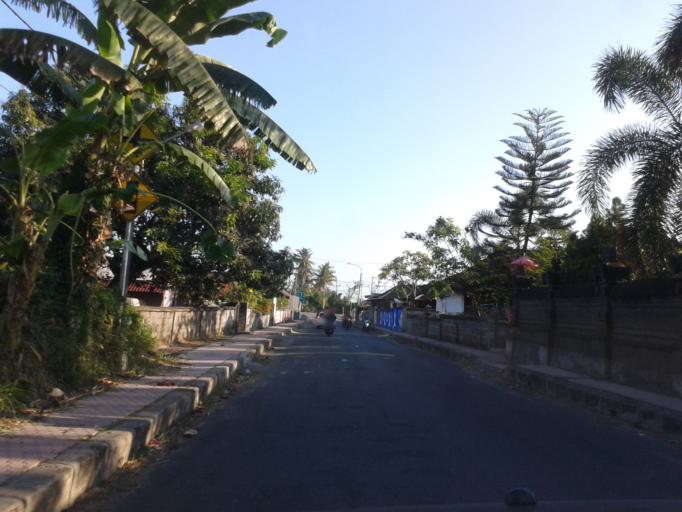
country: ID
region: Bali
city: Semarapura
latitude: -8.5670
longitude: 115.3849
